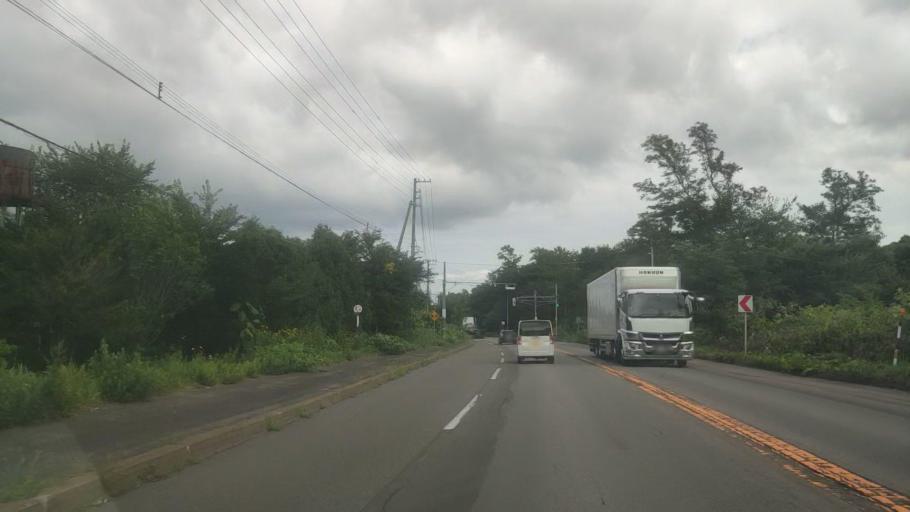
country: JP
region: Hokkaido
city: Nanae
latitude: 42.0662
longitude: 140.6031
